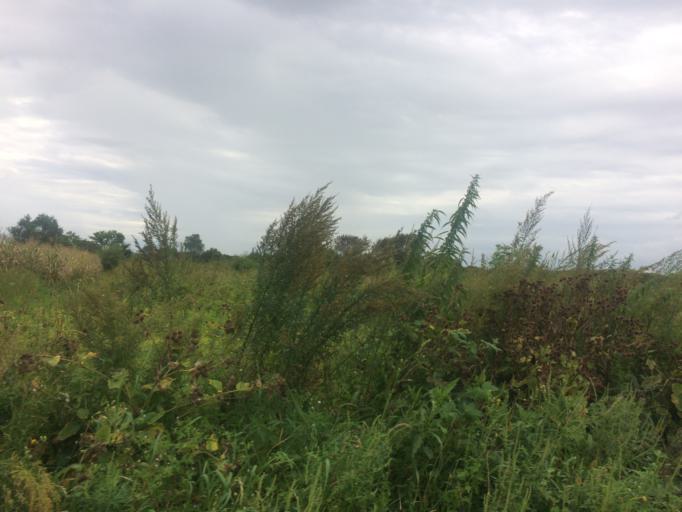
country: RU
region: Primorskiy
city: Lazo
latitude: 45.8321
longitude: 133.6131
